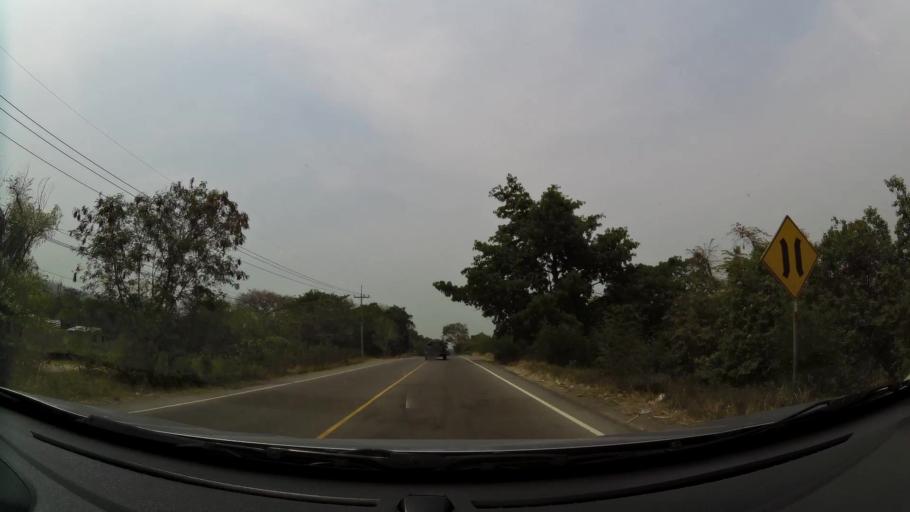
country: HN
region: Cortes
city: Potrerillos
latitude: 15.1854
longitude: -87.9618
